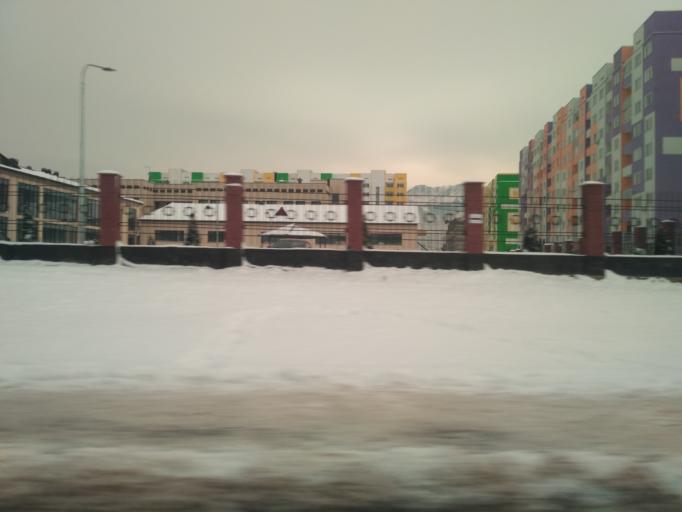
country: KZ
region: Almaty Qalasy
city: Almaty
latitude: 43.2152
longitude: 76.7897
